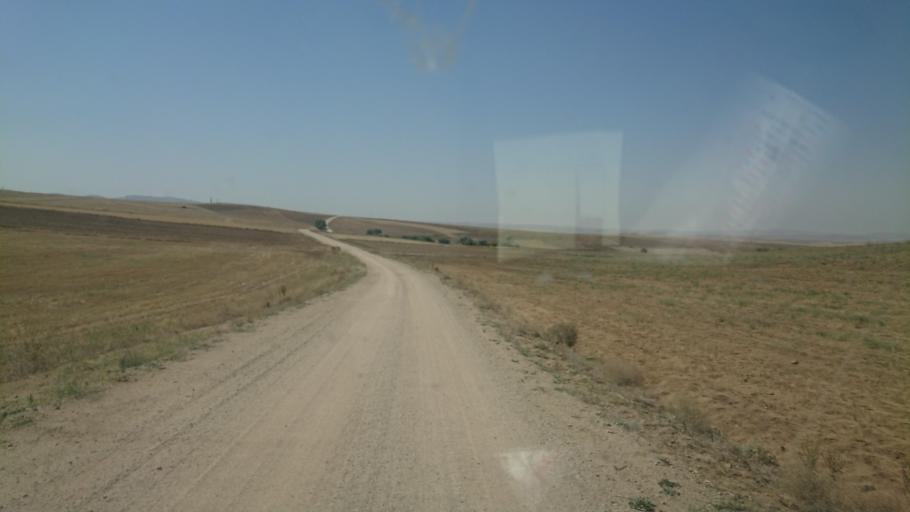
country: TR
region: Aksaray
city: Agacoren
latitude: 38.7949
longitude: 33.9405
